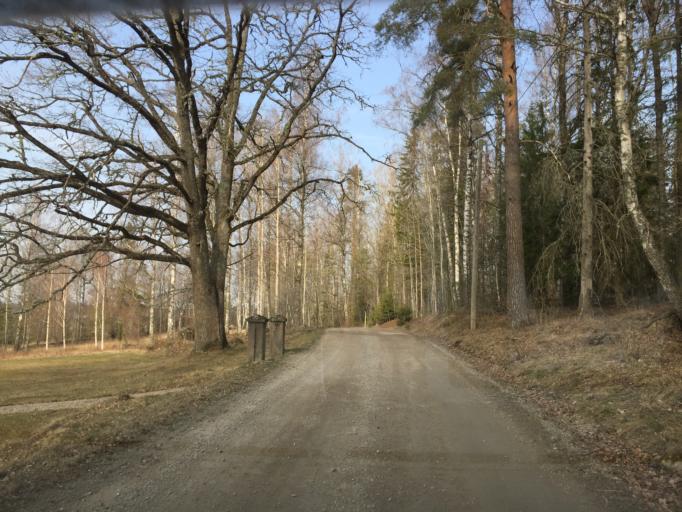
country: SE
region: Soedermanland
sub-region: Vingakers Kommun
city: Vingaker
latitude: 59.0133
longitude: 15.7792
